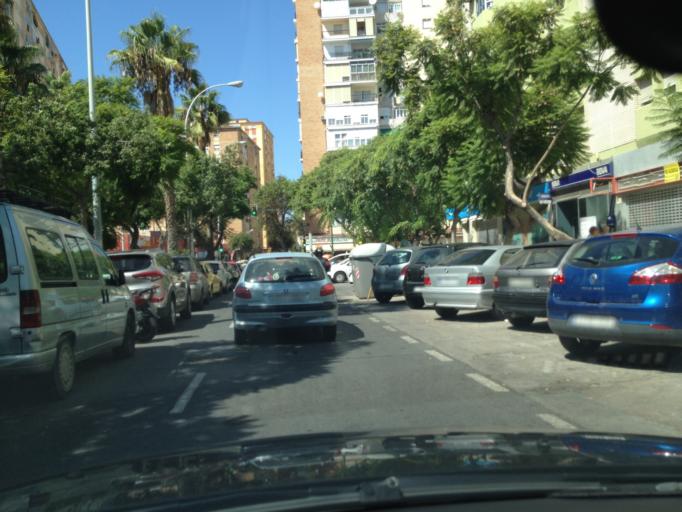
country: ES
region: Andalusia
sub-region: Provincia de Malaga
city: Malaga
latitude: 36.7047
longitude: -4.4360
